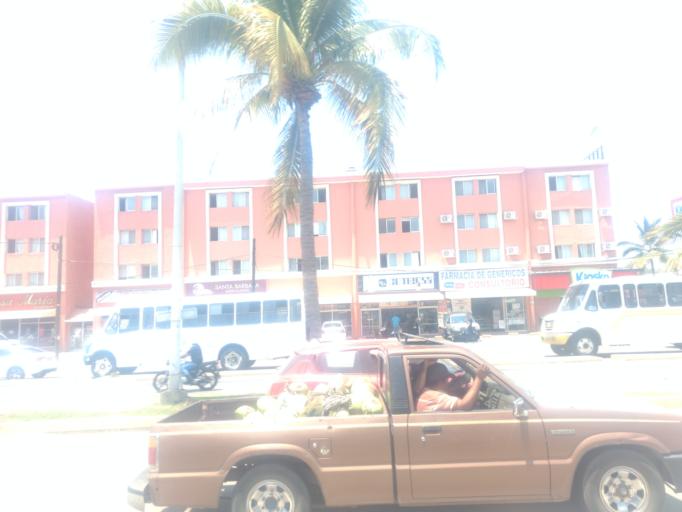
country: MX
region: Colima
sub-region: Manzanillo
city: Manzanillo
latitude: 19.1021
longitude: -104.3271
